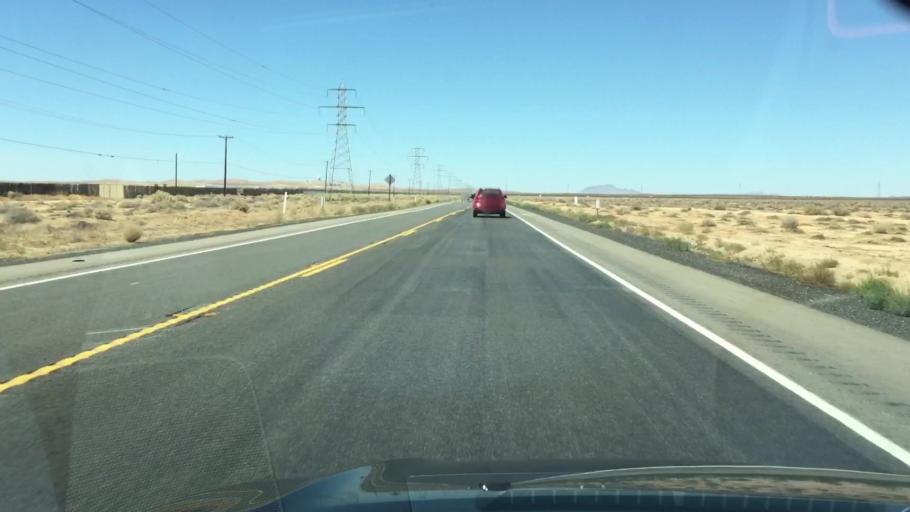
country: US
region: California
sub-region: Kern County
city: Boron
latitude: 35.0137
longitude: -117.5475
